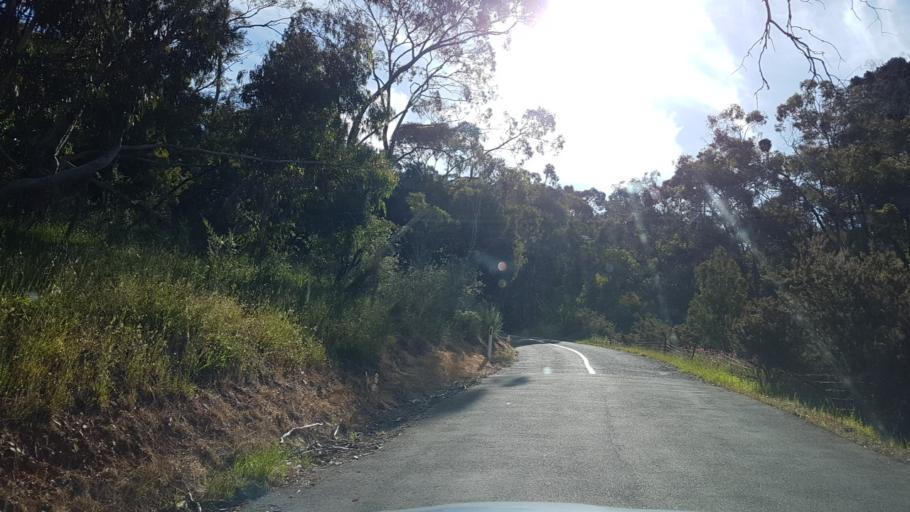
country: AU
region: South Australia
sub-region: Adelaide Hills
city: Adelaide Hills
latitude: -34.9101
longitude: 138.7703
